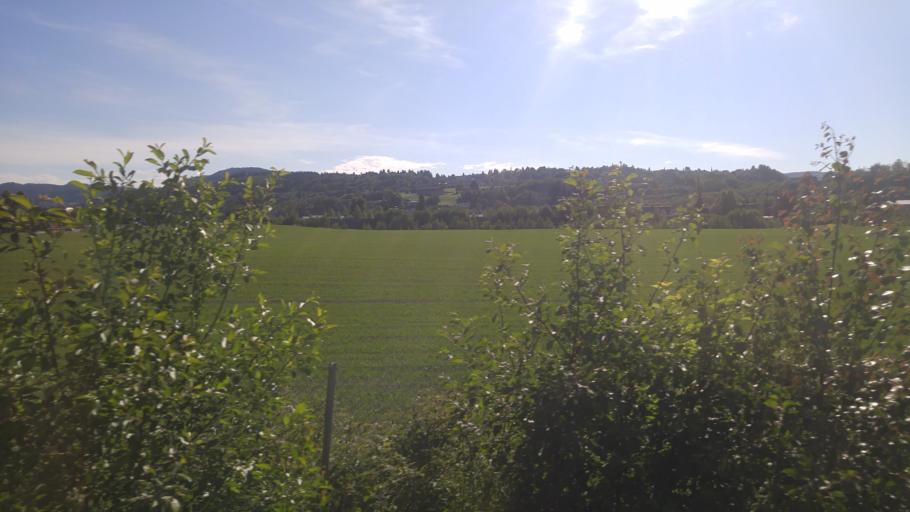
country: NO
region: Sor-Trondelag
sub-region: Melhus
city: Melhus
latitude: 63.2836
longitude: 10.2777
